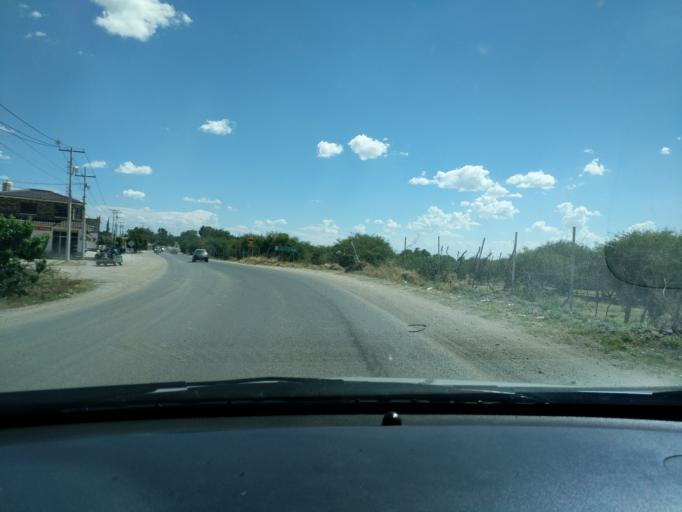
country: MX
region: Guanajuato
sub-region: Leon
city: Ladrilleras del Refugio
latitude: 21.0749
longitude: -101.5473
